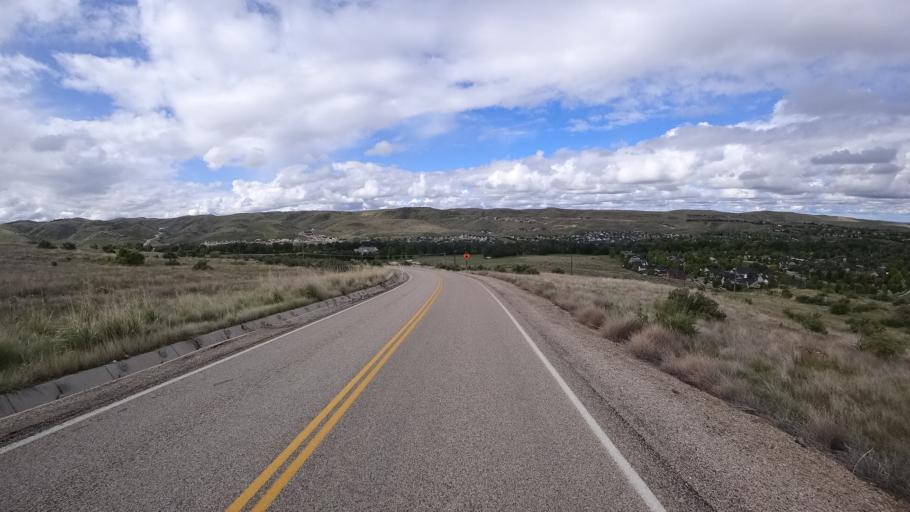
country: US
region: Idaho
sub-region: Ada County
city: Garden City
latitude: 43.7203
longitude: -116.2346
